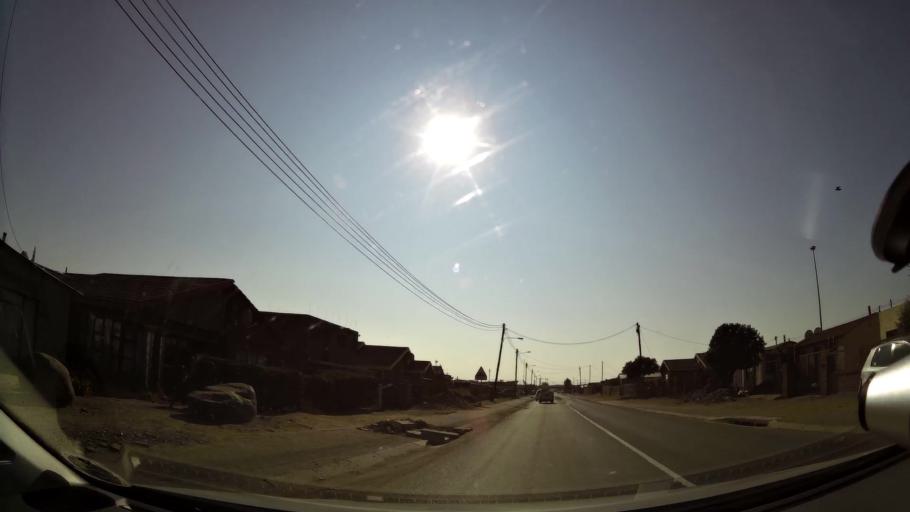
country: ZA
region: Orange Free State
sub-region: Mangaung Metropolitan Municipality
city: Bloemfontein
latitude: -29.1913
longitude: 26.2323
